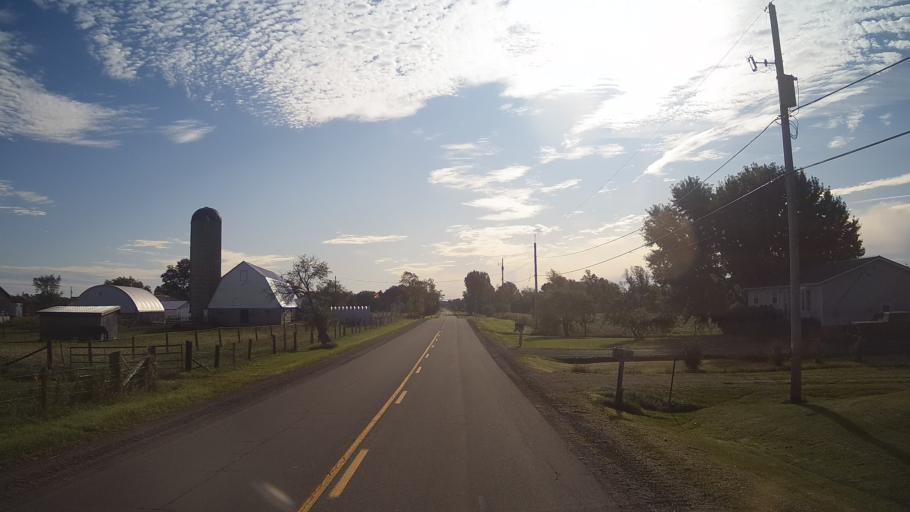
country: CA
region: Ontario
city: Gananoque
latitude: 44.4007
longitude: -76.0852
